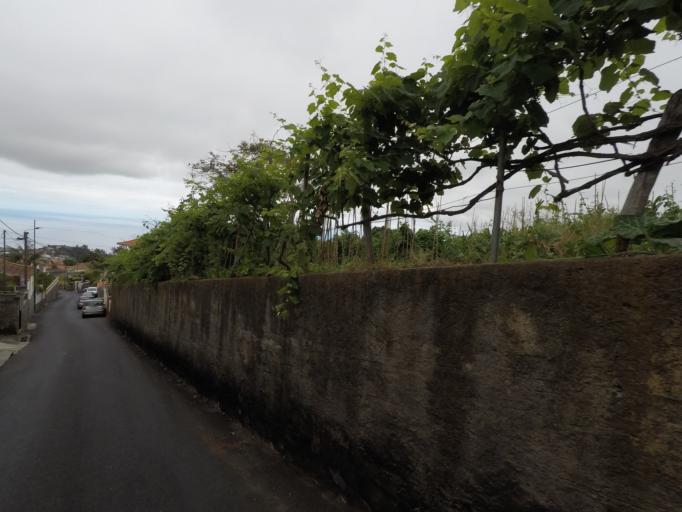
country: PT
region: Madeira
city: Camara de Lobos
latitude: 32.6775
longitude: -16.9498
